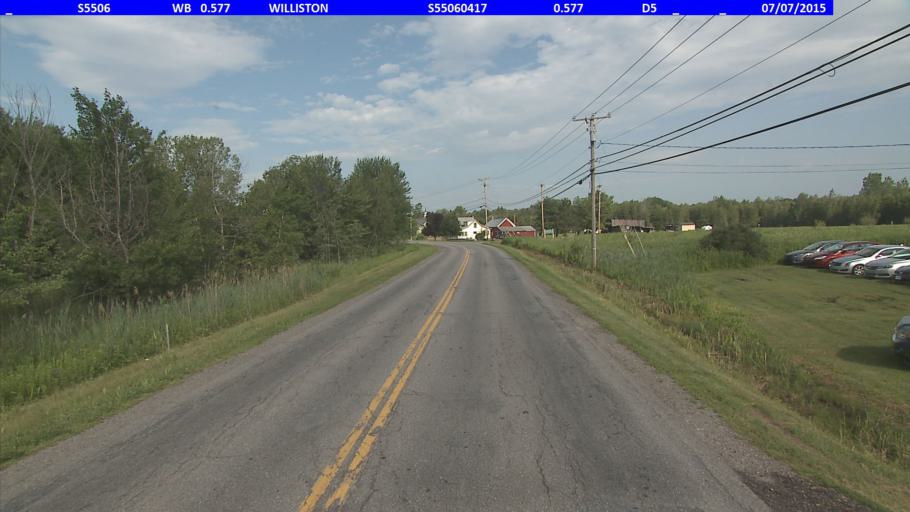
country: US
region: Vermont
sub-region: Chittenden County
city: Essex Junction
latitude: 44.4649
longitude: -73.1018
